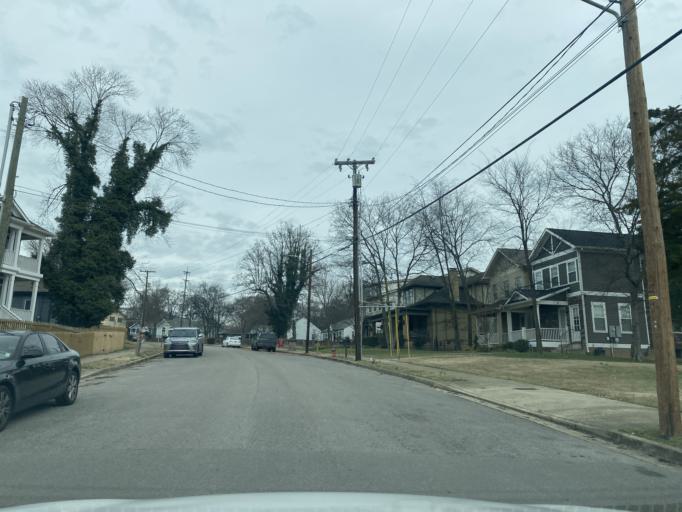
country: US
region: Tennessee
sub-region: Davidson County
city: Nashville
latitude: 36.1354
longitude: -86.7823
